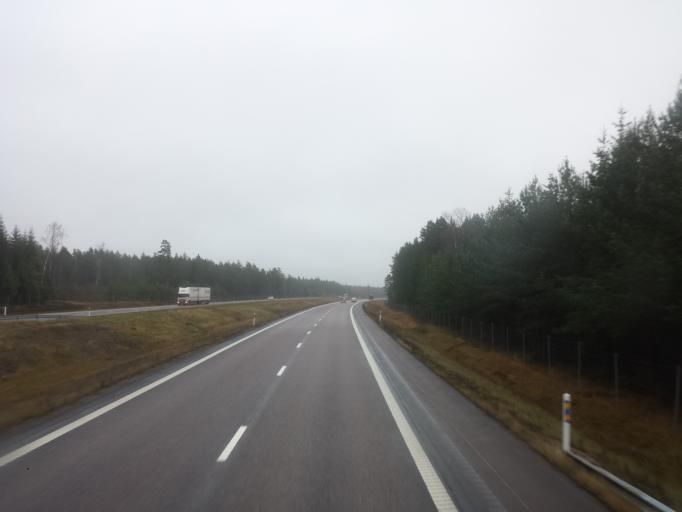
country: SE
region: Soedermanland
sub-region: Nykopings Kommun
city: Stigtomta
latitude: 58.7584
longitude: 16.7959
